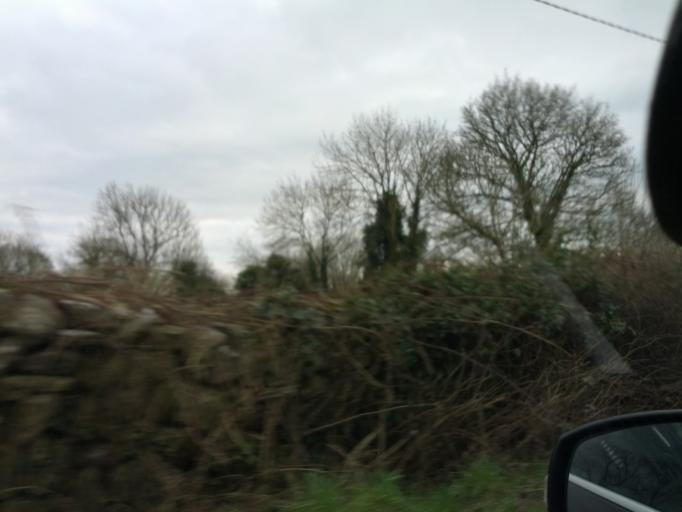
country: IE
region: Connaught
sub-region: County Galway
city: Athenry
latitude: 53.2557
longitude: -8.7407
